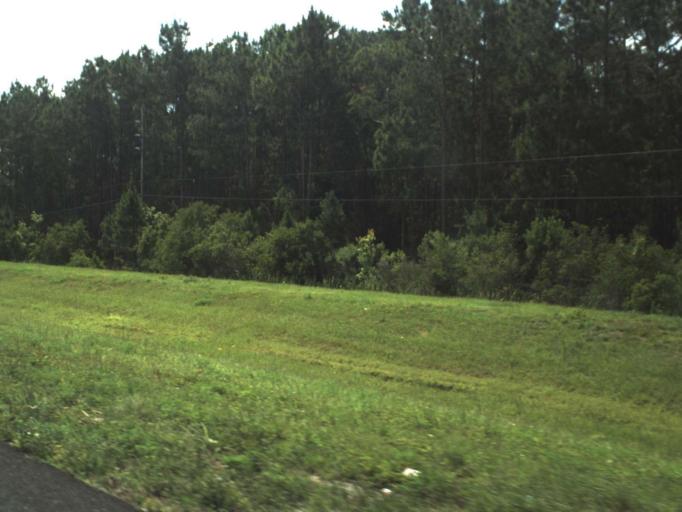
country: US
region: Florida
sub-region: Volusia County
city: Samsula-Spruce Creek
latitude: 29.0113
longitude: -81.0581
